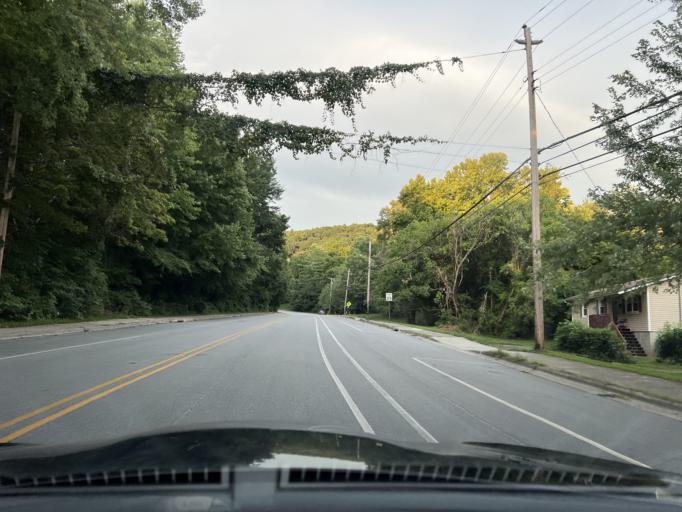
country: US
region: North Carolina
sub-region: Buncombe County
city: Asheville
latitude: 35.5907
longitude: -82.5476
